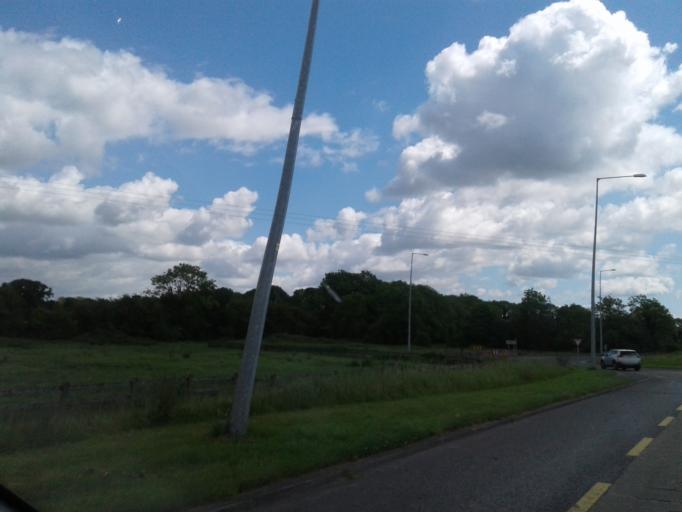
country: IE
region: Leinster
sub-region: Uibh Fhaili
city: Tullamore
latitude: 53.2893
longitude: -7.4916
